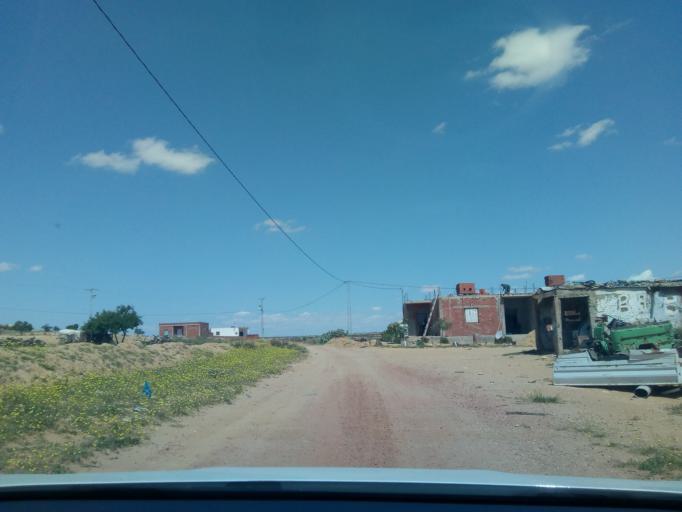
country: TN
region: Safaqis
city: Sfax
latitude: 34.7291
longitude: 10.4984
